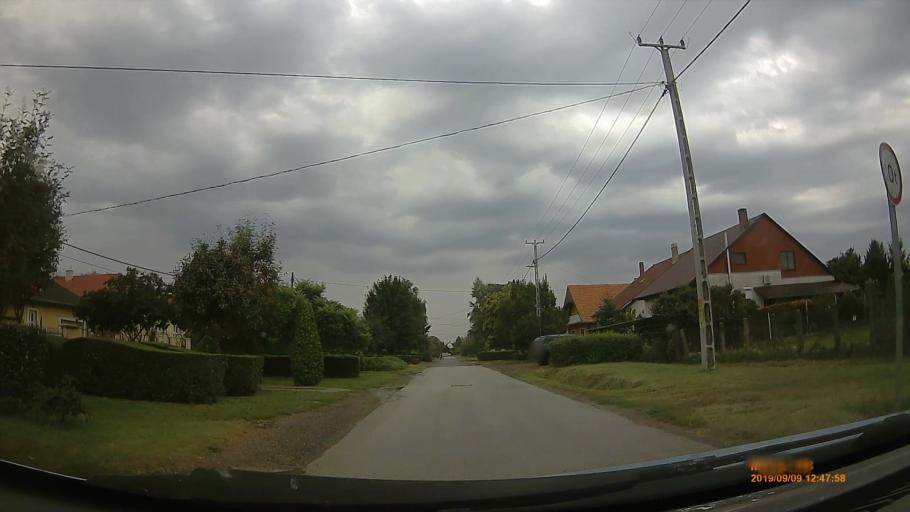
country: HU
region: Szabolcs-Szatmar-Bereg
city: Nyirpazony
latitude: 47.9475
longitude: 21.7941
